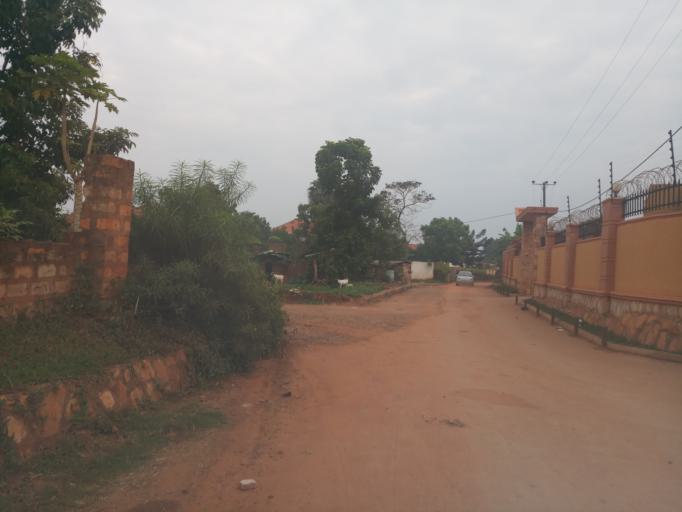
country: UG
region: Central Region
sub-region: Wakiso District
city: Kireka
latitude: 0.3923
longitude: 32.6353
